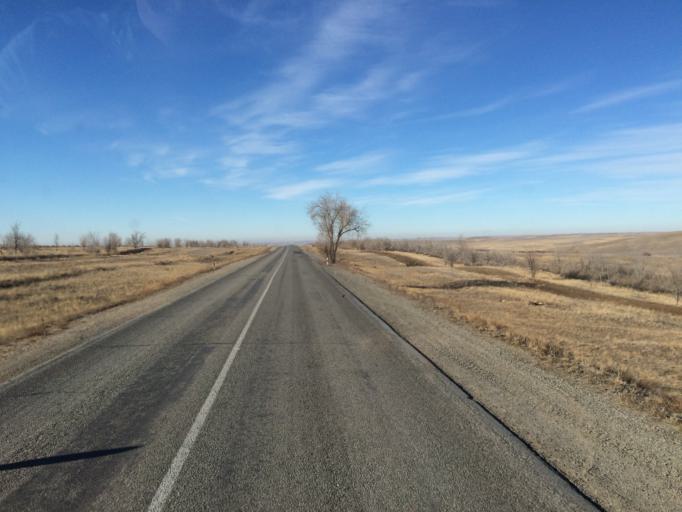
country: KZ
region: Aqtoebe
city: Aqtobe
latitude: 50.2829
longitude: 57.7411
